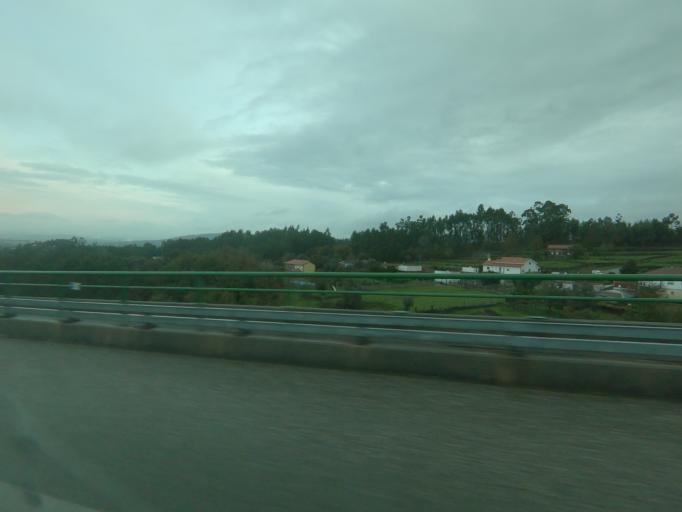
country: PT
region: Viana do Castelo
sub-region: Vila Nova de Cerveira
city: Vila Nova de Cerveira
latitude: 41.9527
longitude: -8.6723
